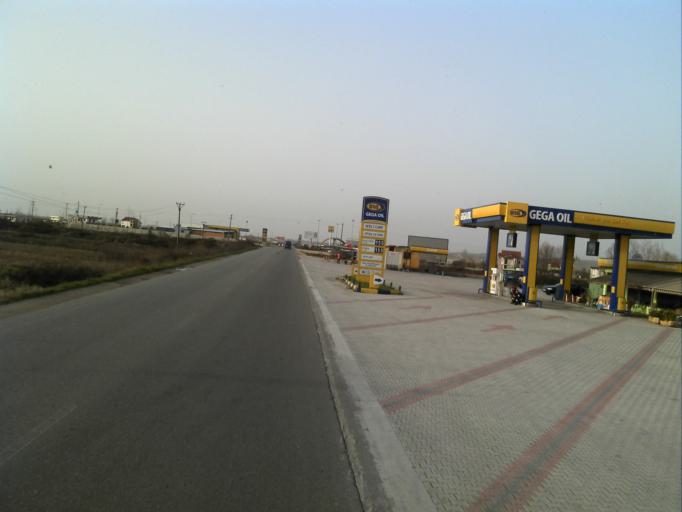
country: AL
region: Durres
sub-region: Rrethi i Krujes
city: Hasan
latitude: 41.5147
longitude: 19.6905
